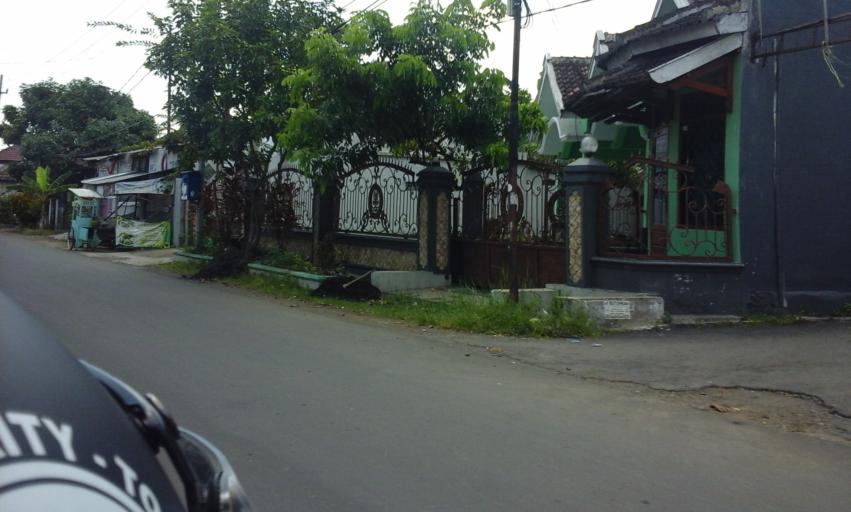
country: ID
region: East Java
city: Kaliwates
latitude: -8.1767
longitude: 113.6781
